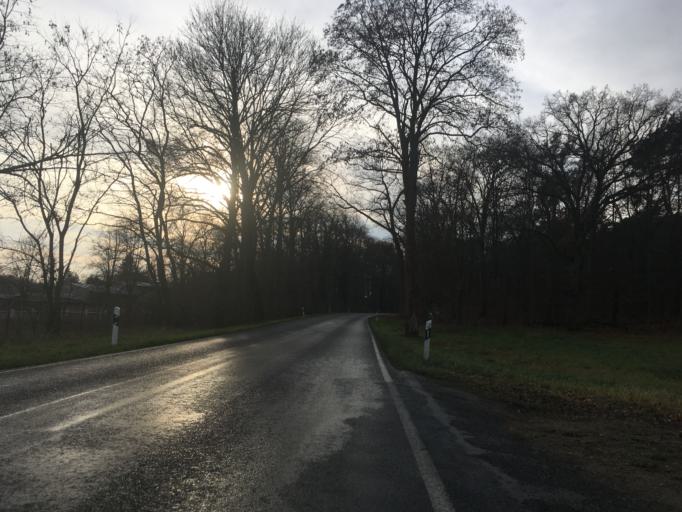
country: DE
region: Brandenburg
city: Eberswalde
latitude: 52.8497
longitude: 13.8470
